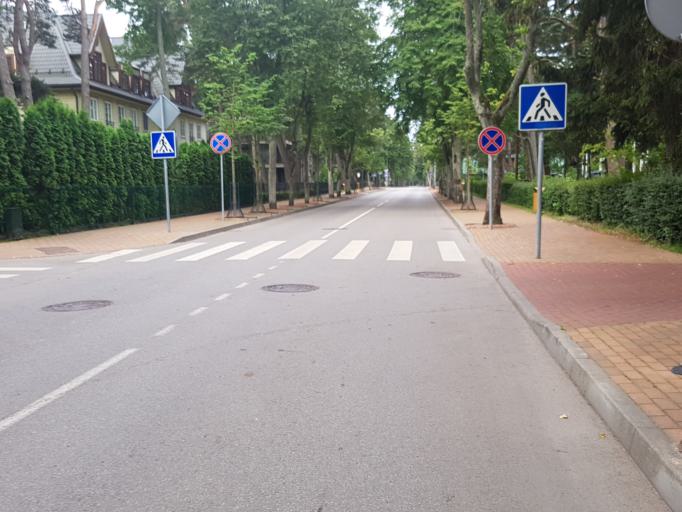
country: LT
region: Klaipedos apskritis
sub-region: Klaipeda
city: Palanga
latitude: 55.9161
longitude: 21.0575
